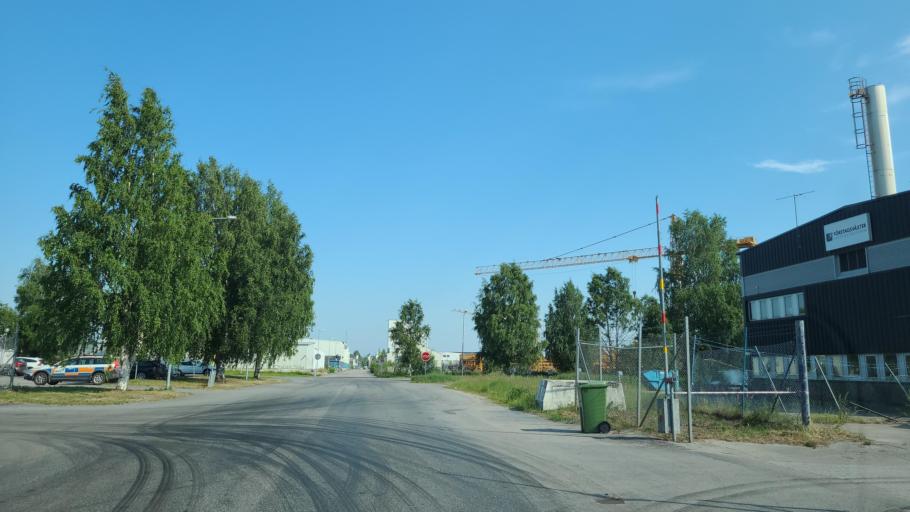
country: SE
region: Vaesterbotten
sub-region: Umea Kommun
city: Umea
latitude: 63.8440
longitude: 20.2243
